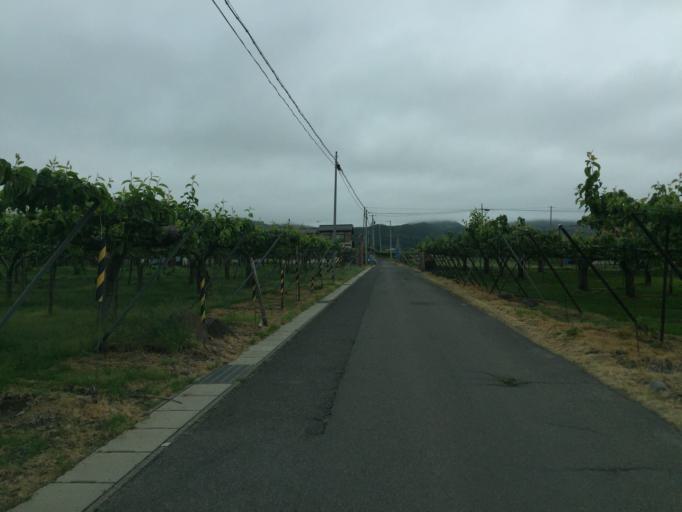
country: JP
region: Fukushima
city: Fukushima-shi
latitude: 37.7783
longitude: 140.3926
